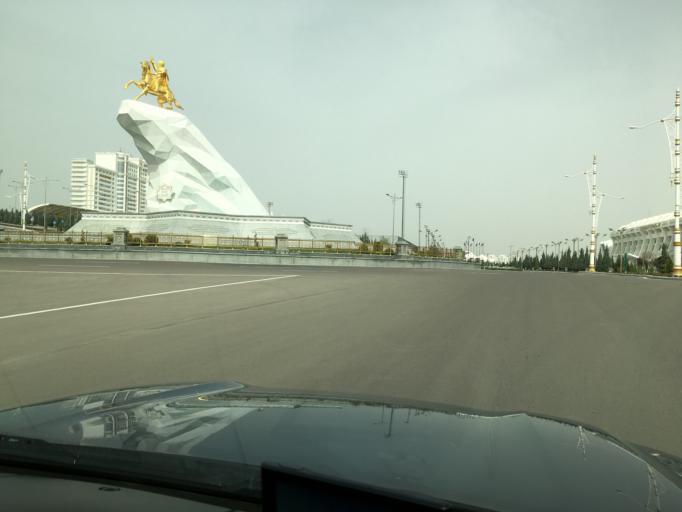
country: TM
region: Ahal
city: Ashgabat
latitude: 37.9250
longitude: 58.3493
